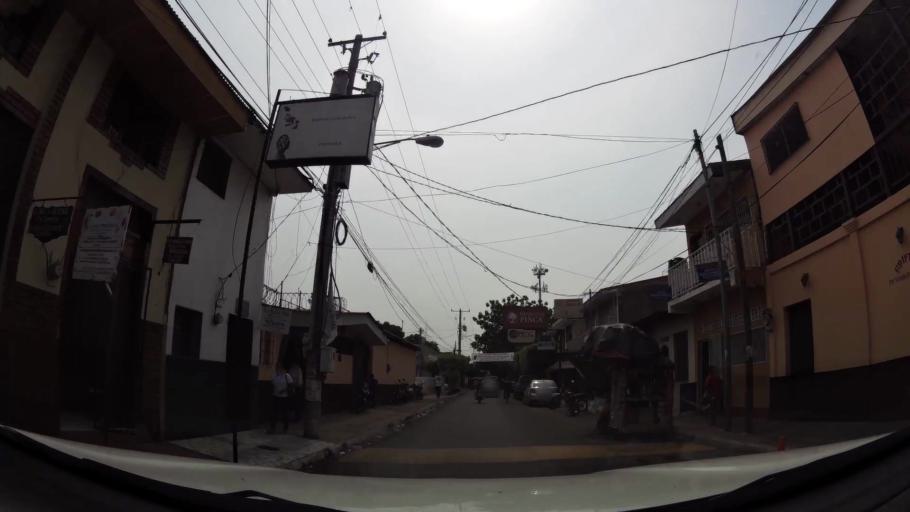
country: NI
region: Chinandega
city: Chinandega
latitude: 12.6296
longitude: -87.1318
